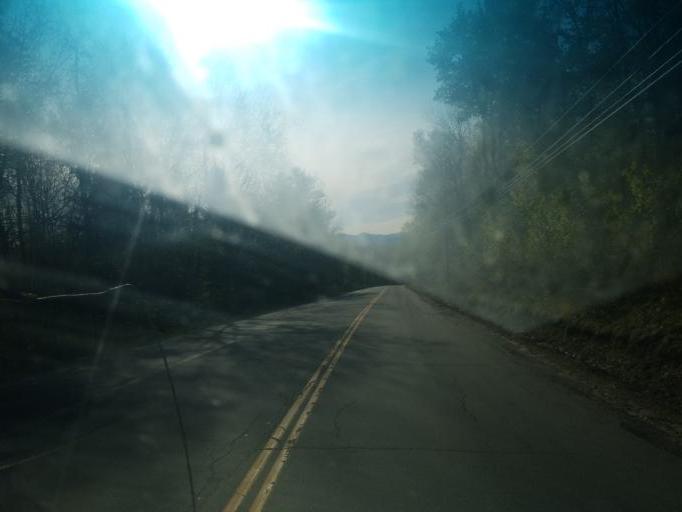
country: US
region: New Hampshire
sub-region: Grafton County
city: Deerfield
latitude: 44.2820
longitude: -71.6533
